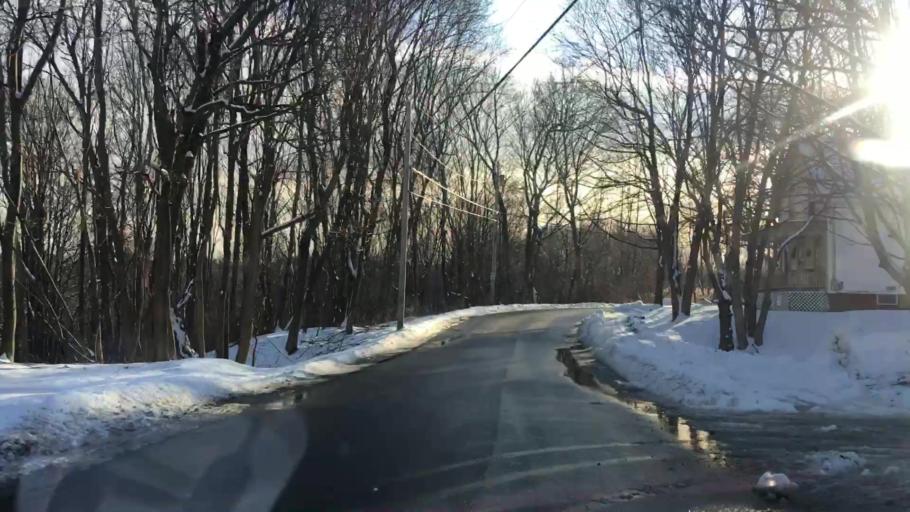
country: US
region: Maine
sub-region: Kennebec County
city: Gardiner
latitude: 44.2287
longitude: -69.7832
